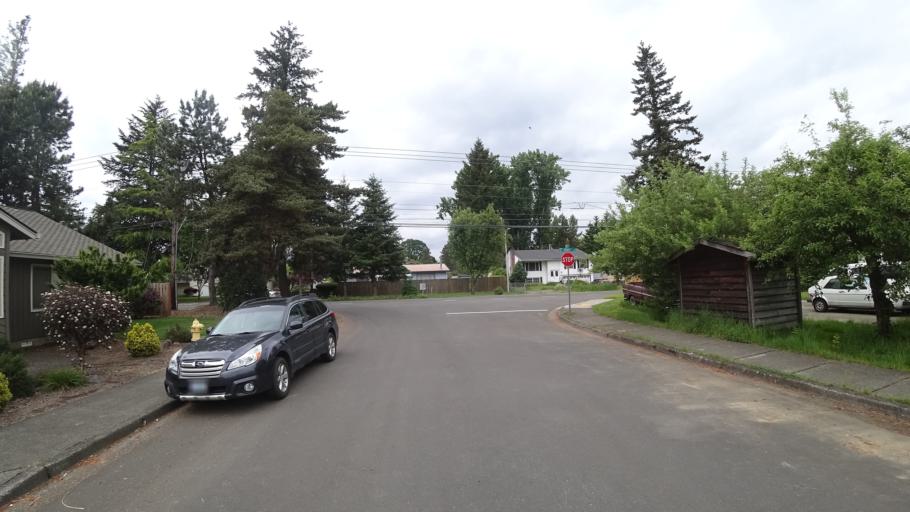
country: US
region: Oregon
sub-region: Washington County
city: Raleigh Hills
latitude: 45.4691
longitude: -122.7799
